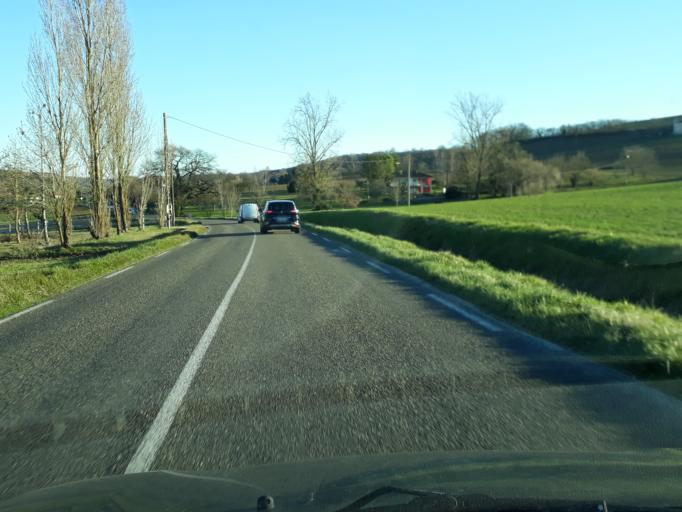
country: FR
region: Midi-Pyrenees
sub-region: Departement du Gers
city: Pavie
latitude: 43.6239
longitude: 0.6386
